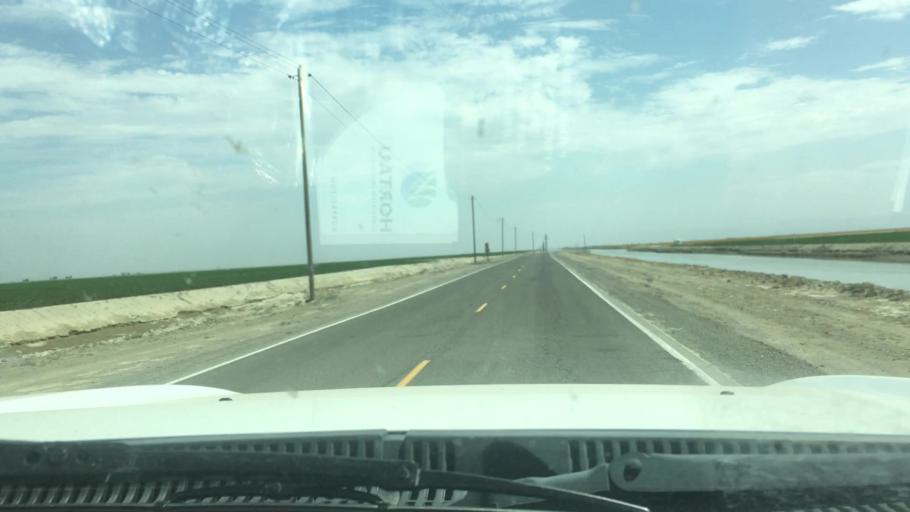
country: US
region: California
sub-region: Tulare County
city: Alpaugh
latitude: 35.8951
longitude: -119.5734
